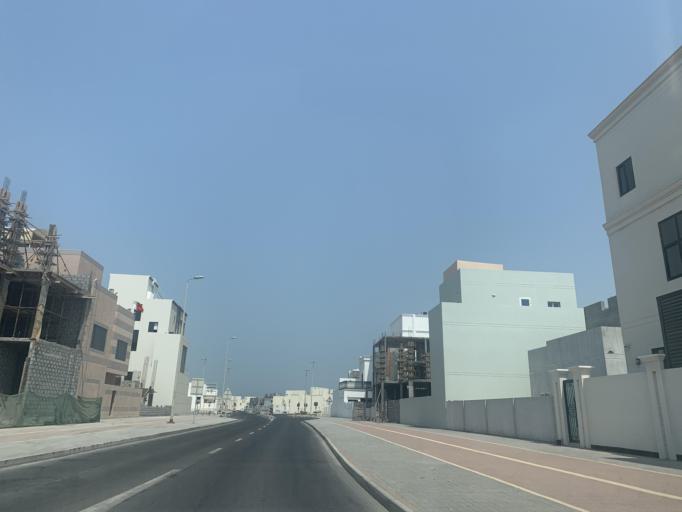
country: BH
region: Muharraq
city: Al Hadd
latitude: 26.2394
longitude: 50.6616
